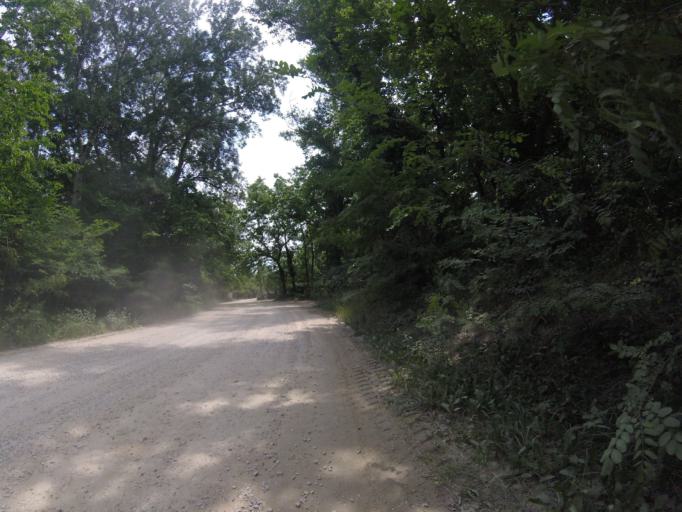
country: HU
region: Pest
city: Leanyfalu
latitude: 47.7186
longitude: 19.1094
